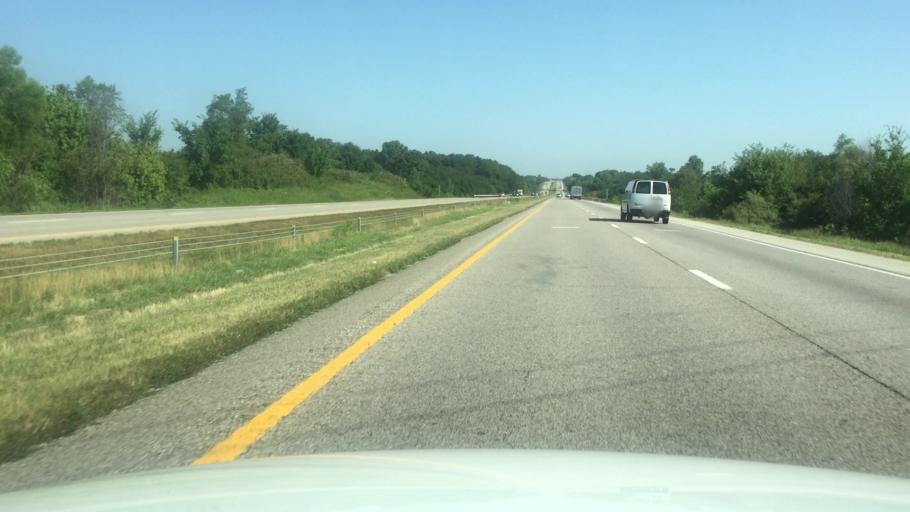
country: US
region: Missouri
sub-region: Platte County
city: Weston
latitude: 39.5594
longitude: -94.7880
